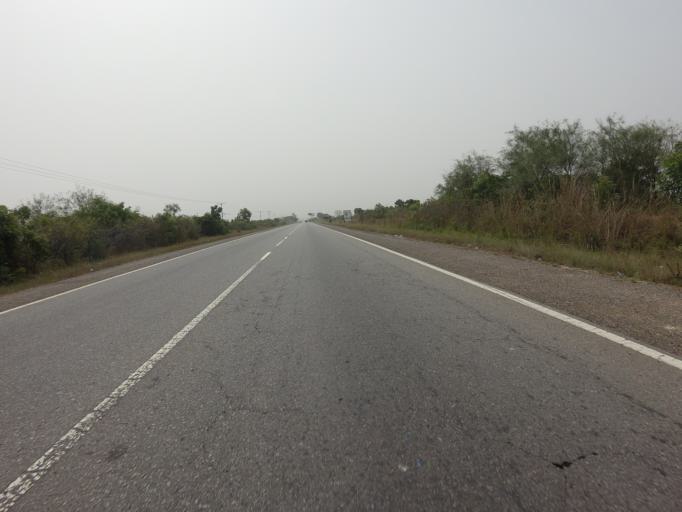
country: GH
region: Volta
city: Anloga
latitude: 5.9735
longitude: 0.5248
